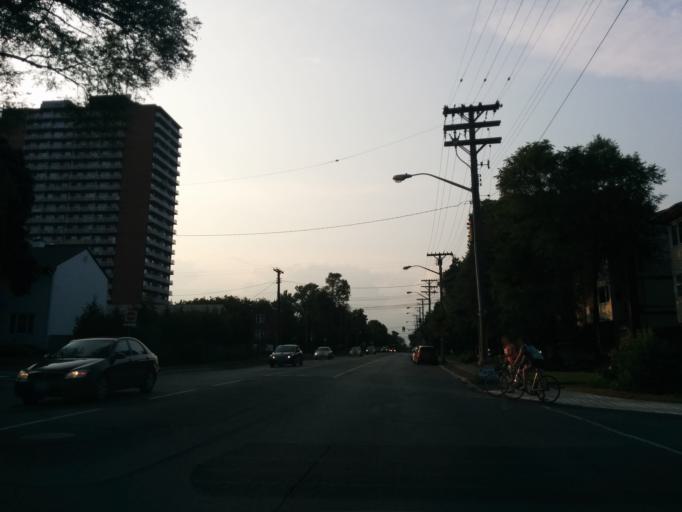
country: CA
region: Ontario
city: Ottawa
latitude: 45.3861
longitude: -75.7412
